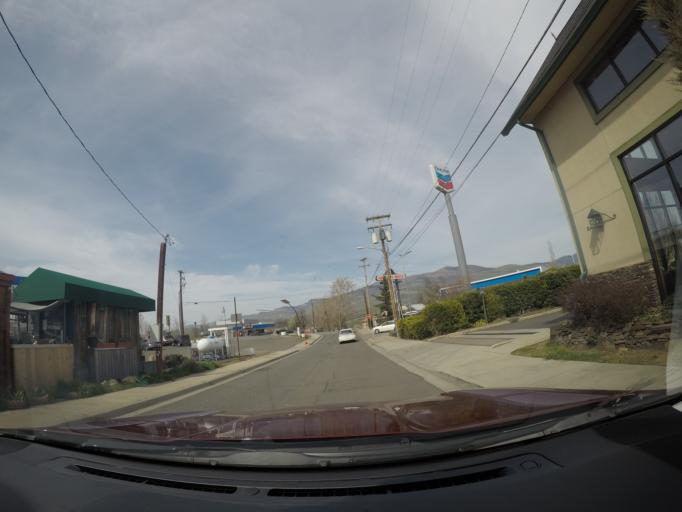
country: US
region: Oregon
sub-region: Jackson County
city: Ashland
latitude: 42.1848
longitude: -122.6640
